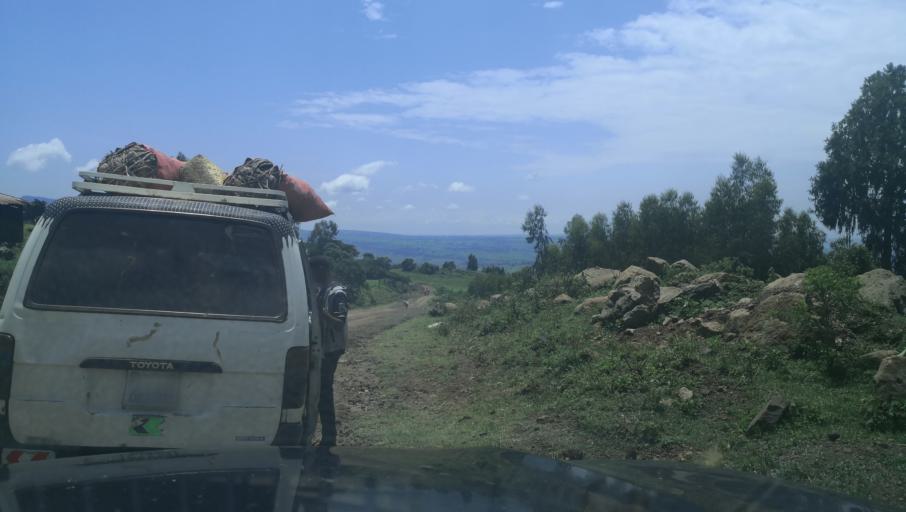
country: ET
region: Southern Nations, Nationalities, and People's Region
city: Butajira
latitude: 8.2744
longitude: 38.4848
